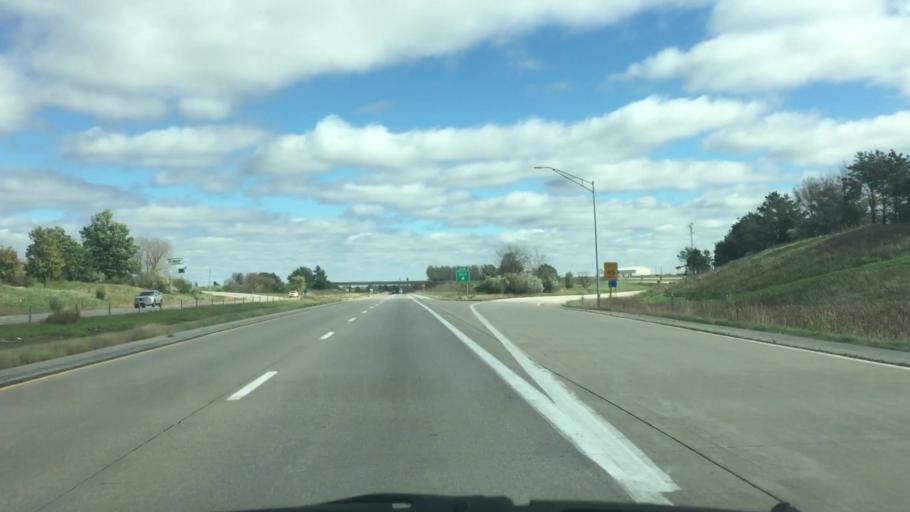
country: US
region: Iowa
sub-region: Iowa County
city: Williamsburg
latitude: 41.6893
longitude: -92.0731
